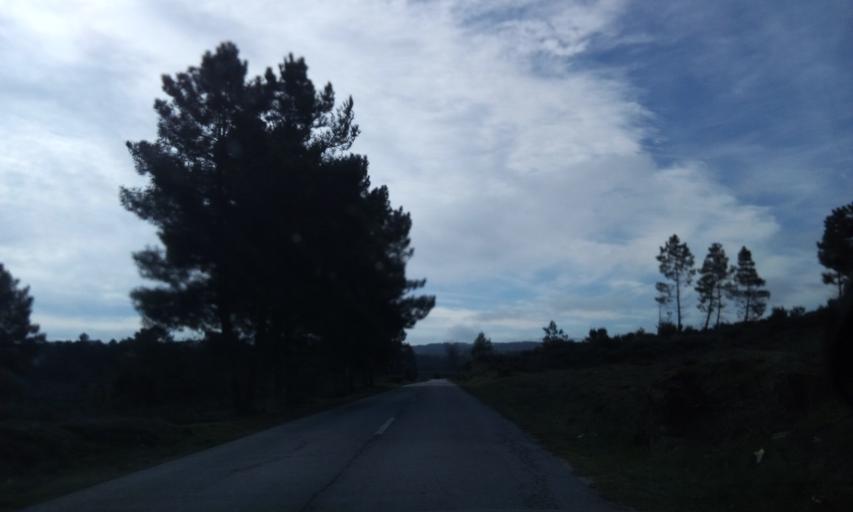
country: PT
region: Guarda
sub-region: Fornos de Algodres
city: Fornos de Algodres
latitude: 40.6739
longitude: -7.5291
